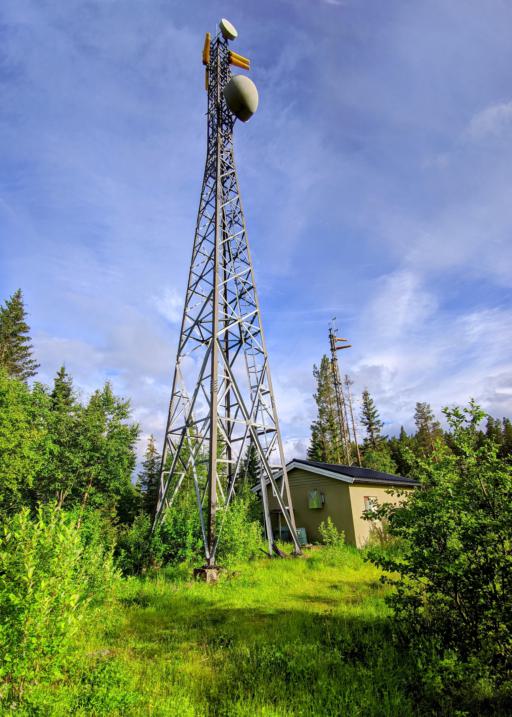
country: NO
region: Buskerud
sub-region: Gol
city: Gol
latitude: 60.7138
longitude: 8.9683
